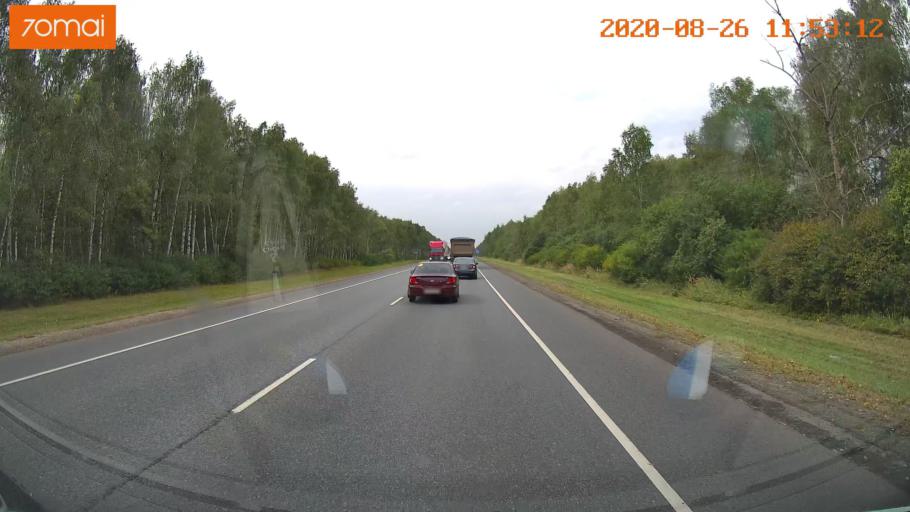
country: RU
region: Rjazan
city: Kiritsy
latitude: 54.2917
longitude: 40.4362
